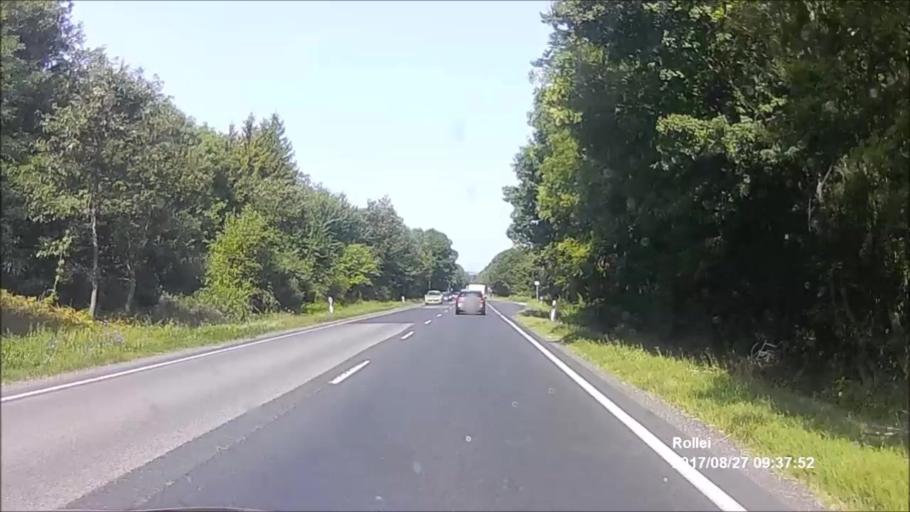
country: HU
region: Gyor-Moson-Sopron
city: Nagycenk
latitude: 47.6191
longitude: 16.6796
